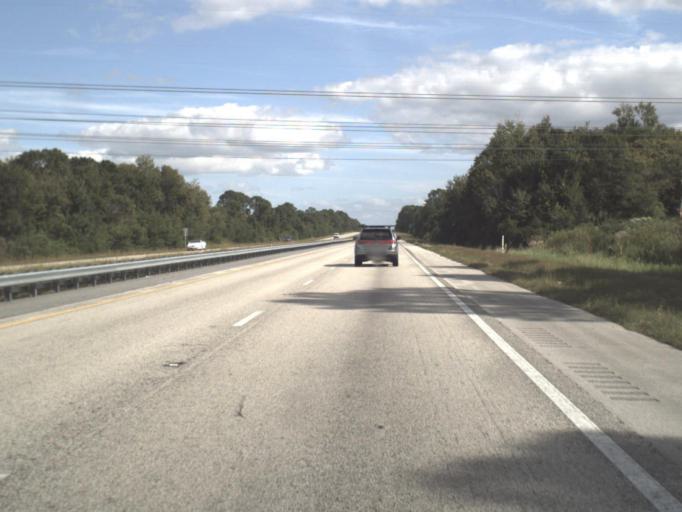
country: US
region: Florida
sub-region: Brevard County
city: Sharpes
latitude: 28.4083
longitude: -80.7941
